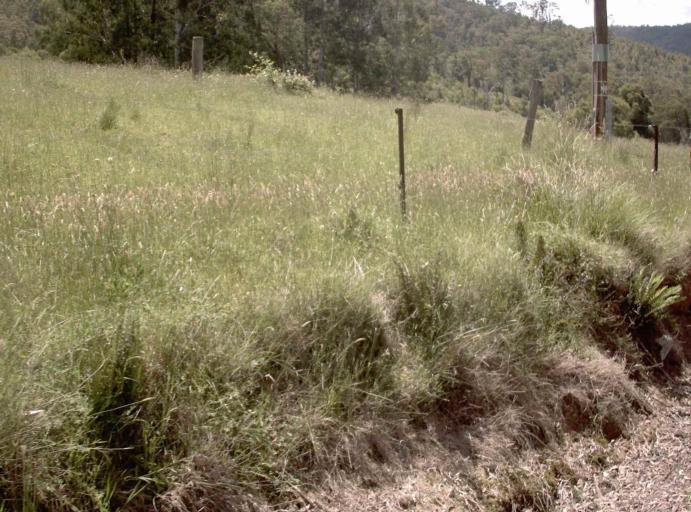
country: AU
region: New South Wales
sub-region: Bombala
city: Bombala
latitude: -37.3670
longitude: 149.0177
